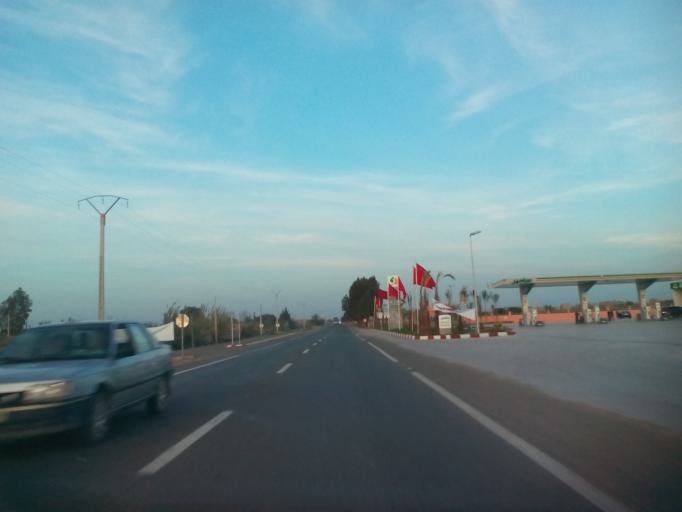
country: MA
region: Marrakech-Tensift-Al Haouz
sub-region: Marrakech
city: Marrakesh
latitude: 31.6271
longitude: -8.2735
